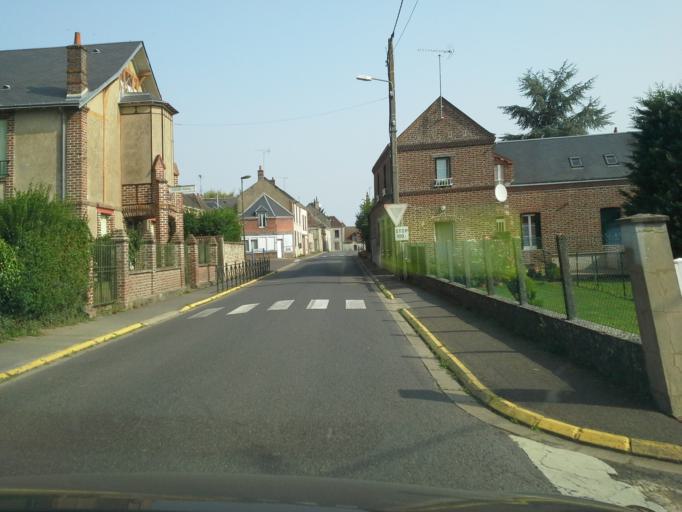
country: FR
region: Centre
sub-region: Departement du Loir-et-Cher
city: Aze
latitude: 47.8915
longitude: 1.0267
